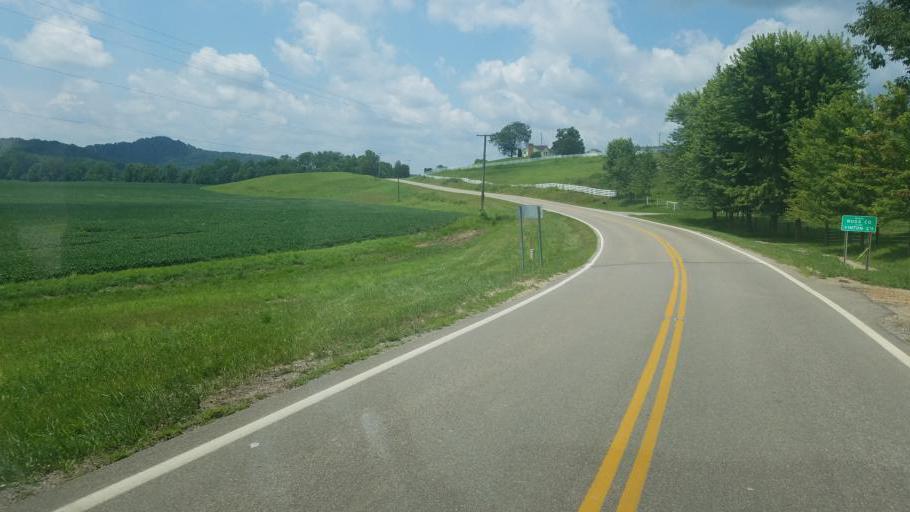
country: US
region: Ohio
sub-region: Ross County
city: Chillicothe
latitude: 39.2899
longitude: -82.7551
